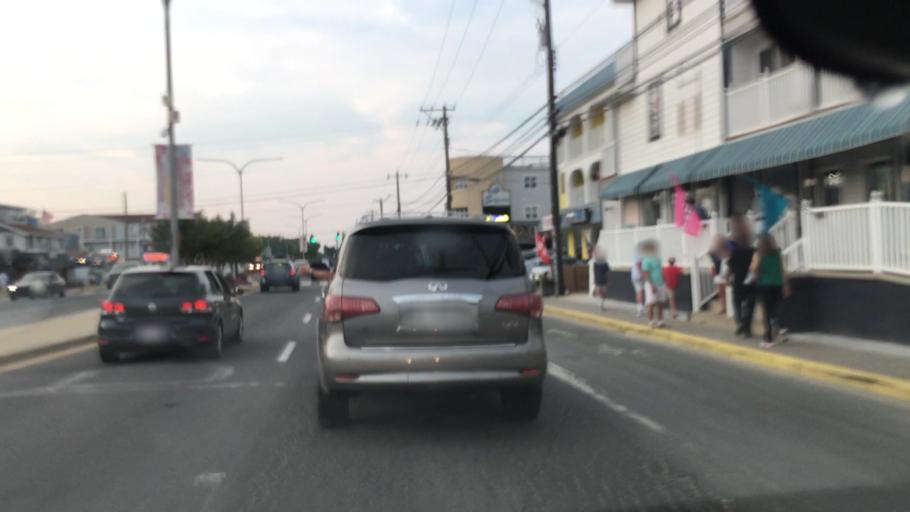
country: US
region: Delaware
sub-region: Sussex County
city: Rehoboth Beach
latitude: 38.6946
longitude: -75.0749
